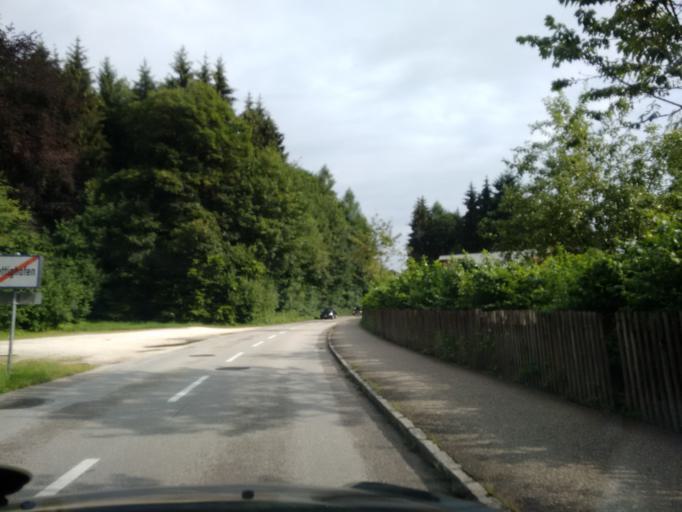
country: AT
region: Upper Austria
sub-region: Politischer Bezirk Vocklabruck
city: Lenzing
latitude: 47.9618
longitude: 13.6076
